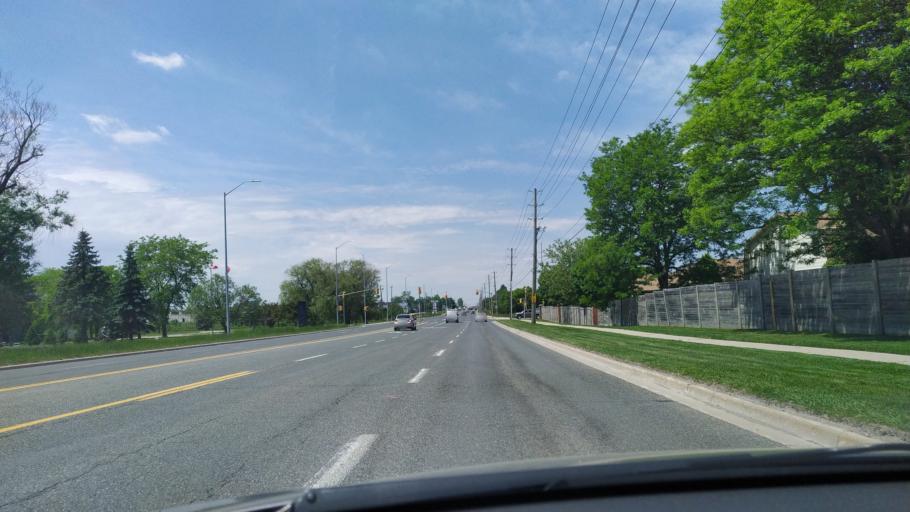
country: CA
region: Ontario
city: London
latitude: 42.9254
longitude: -81.2238
